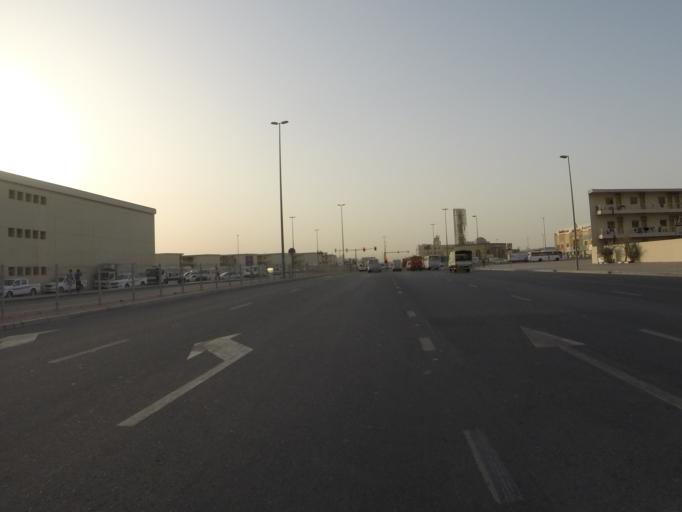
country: AE
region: Dubai
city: Dubai
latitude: 25.1308
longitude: 55.2313
